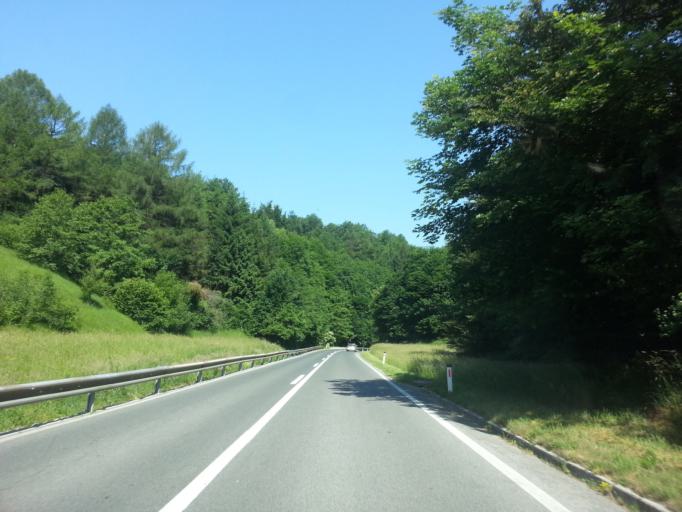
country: SI
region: Ilirska Bistrica
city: Ilirska Bistrica
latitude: 45.5124
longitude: 14.2560
